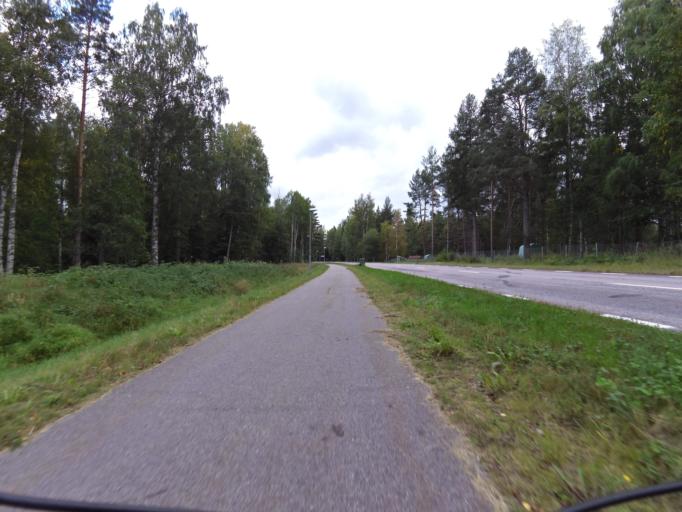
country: SE
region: Gaevleborg
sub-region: Sandvikens Kommun
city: Sandviken
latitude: 60.6904
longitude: 16.8152
